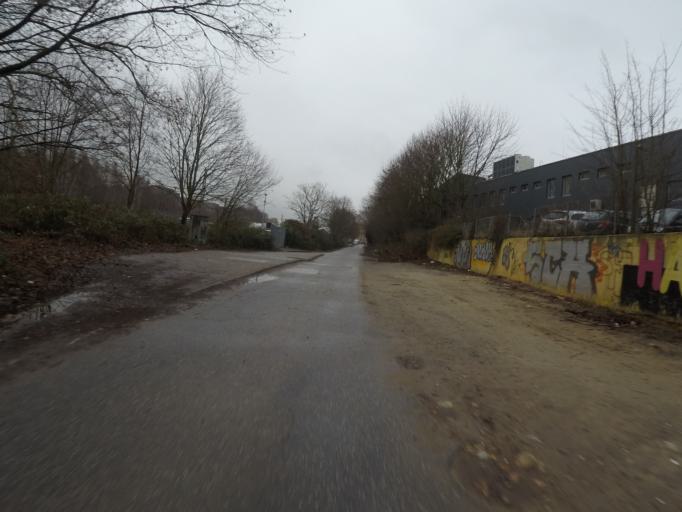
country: DE
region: Hamburg
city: Harburg
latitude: 53.4689
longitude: 9.9693
